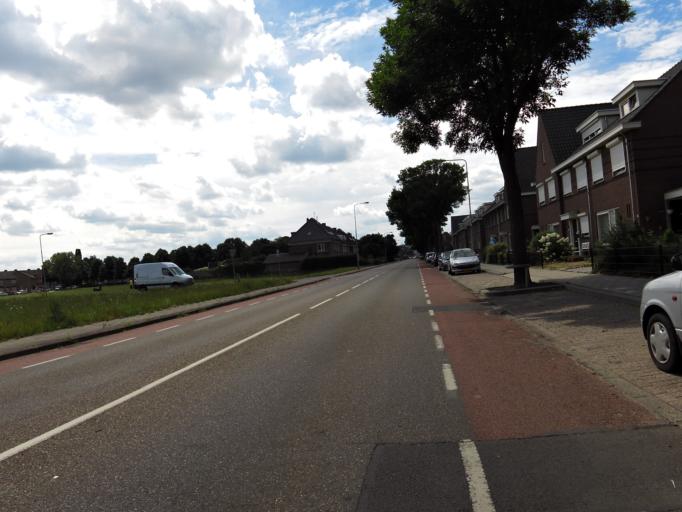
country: NL
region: Limburg
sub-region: Gemeente Sittard-Geleen
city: Sittard
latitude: 51.0057
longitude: 5.8852
